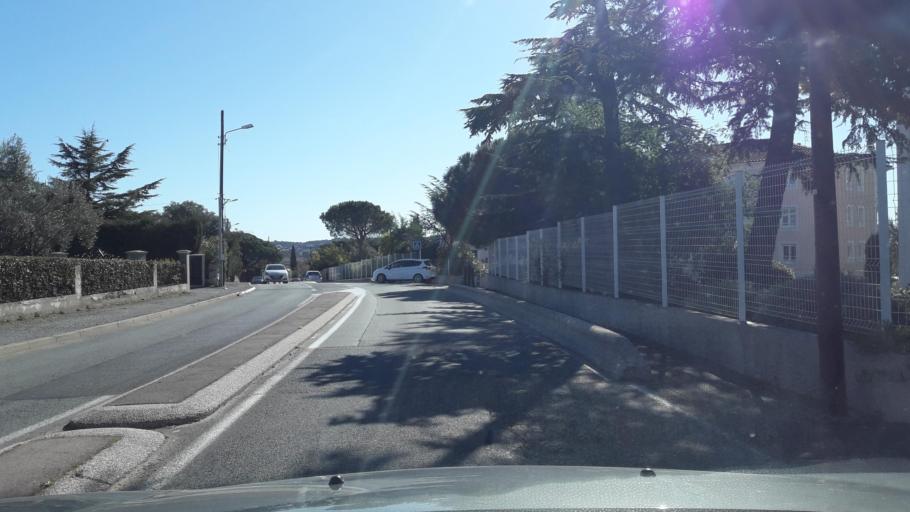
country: FR
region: Provence-Alpes-Cote d'Azur
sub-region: Departement du Var
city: Frejus
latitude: 43.4415
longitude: 6.7538
